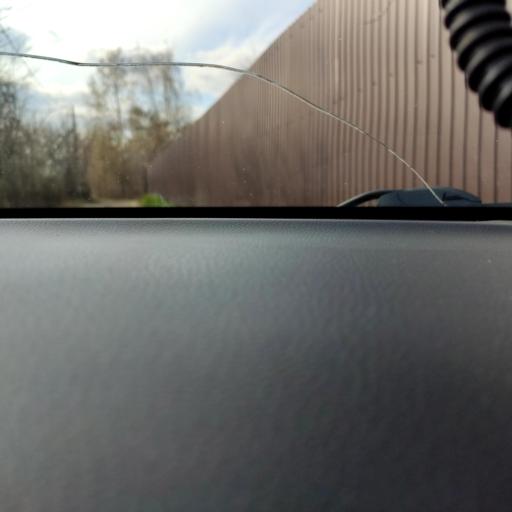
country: RU
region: Tatarstan
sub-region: Gorod Kazan'
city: Kazan
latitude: 55.8878
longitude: 49.0664
